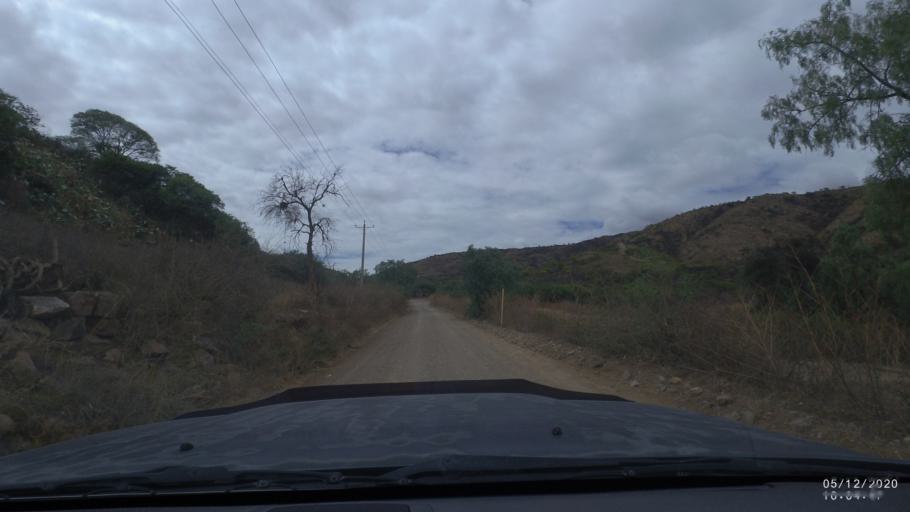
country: BO
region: Cochabamba
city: Sipe Sipe
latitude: -17.4656
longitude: -66.2862
